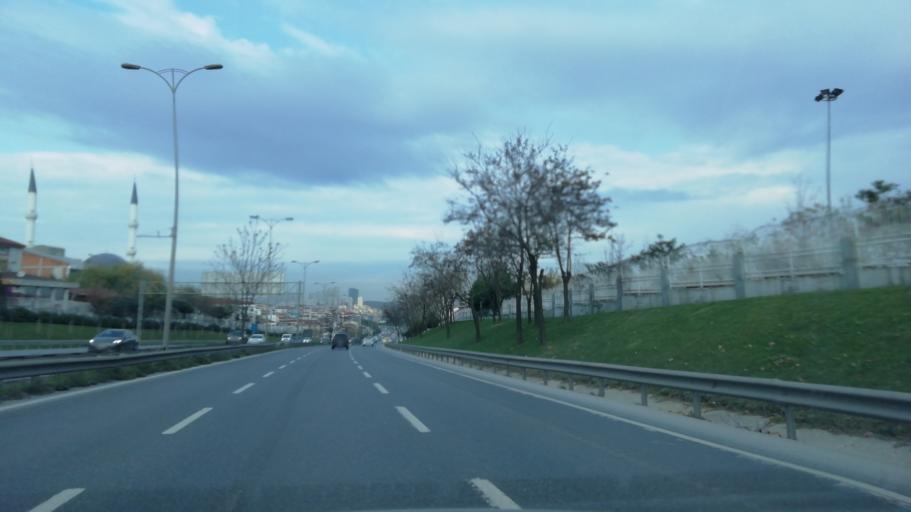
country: TR
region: Istanbul
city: Esenyurt
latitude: 41.0347
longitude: 28.6873
